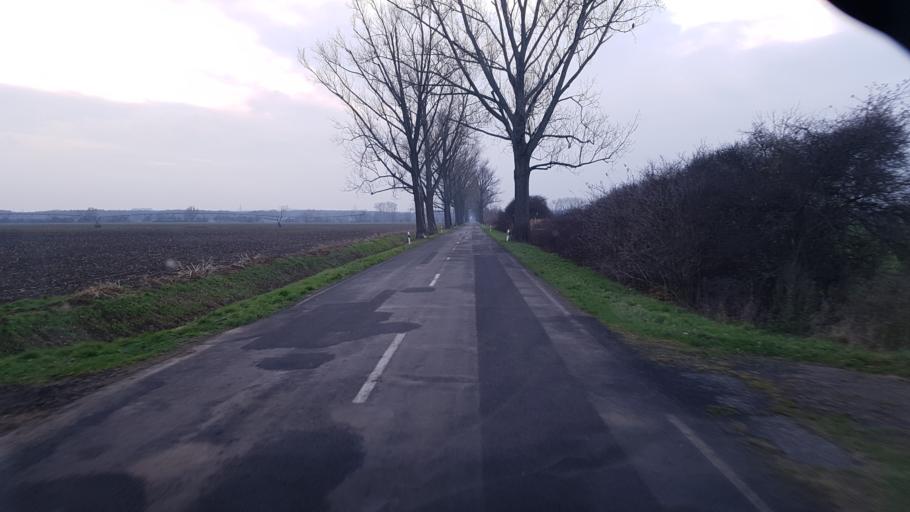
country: DE
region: Brandenburg
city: Ziltendorf
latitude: 52.2158
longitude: 14.6481
